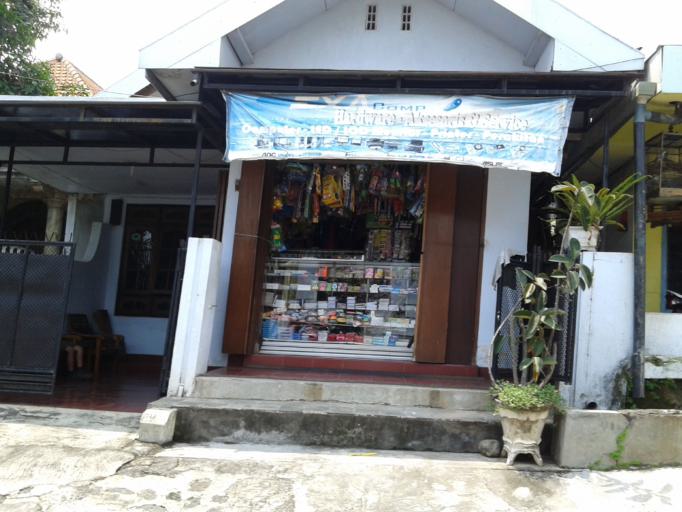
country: ID
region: East Java
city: Lawang
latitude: -7.8236
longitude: 112.7184
